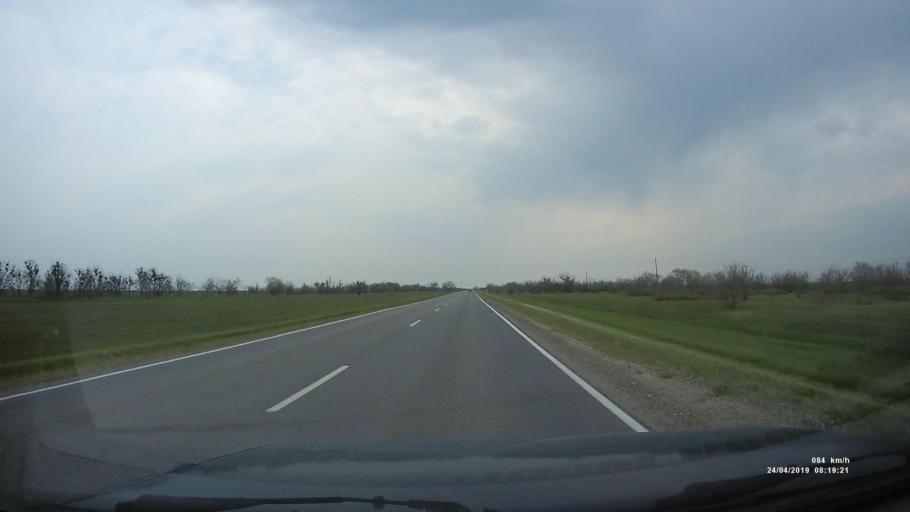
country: RU
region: Kalmykiya
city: Priyutnoye
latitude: 46.1038
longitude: 43.6638
